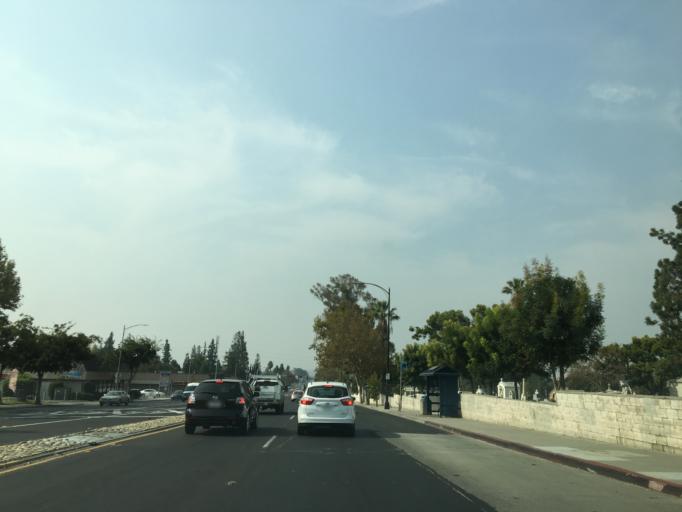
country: US
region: California
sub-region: Santa Clara County
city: Alum Rock
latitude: 37.3623
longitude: -121.8357
